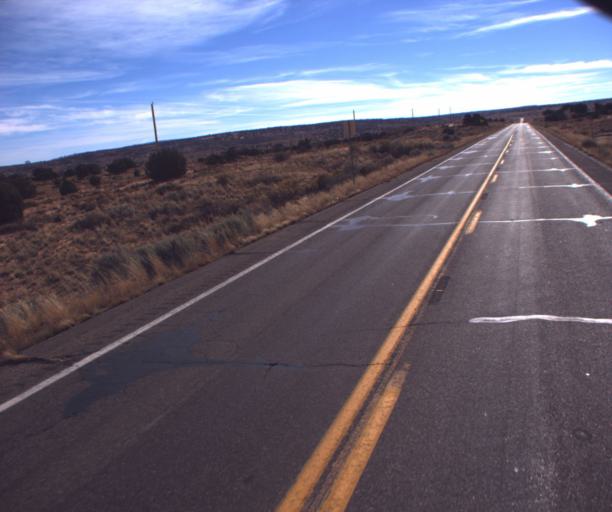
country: US
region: Arizona
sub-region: Coconino County
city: Kaibito
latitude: 36.5966
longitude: -111.1655
